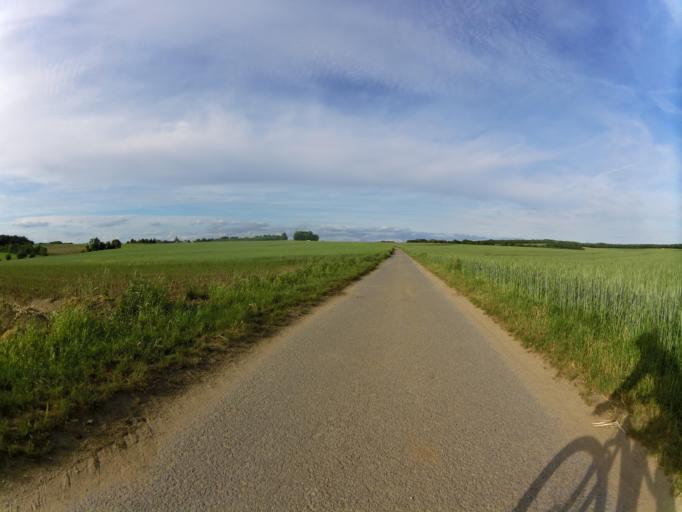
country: DE
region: Bavaria
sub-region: Regierungsbezirk Unterfranken
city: Frickenhausen
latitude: 49.6991
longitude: 10.0743
